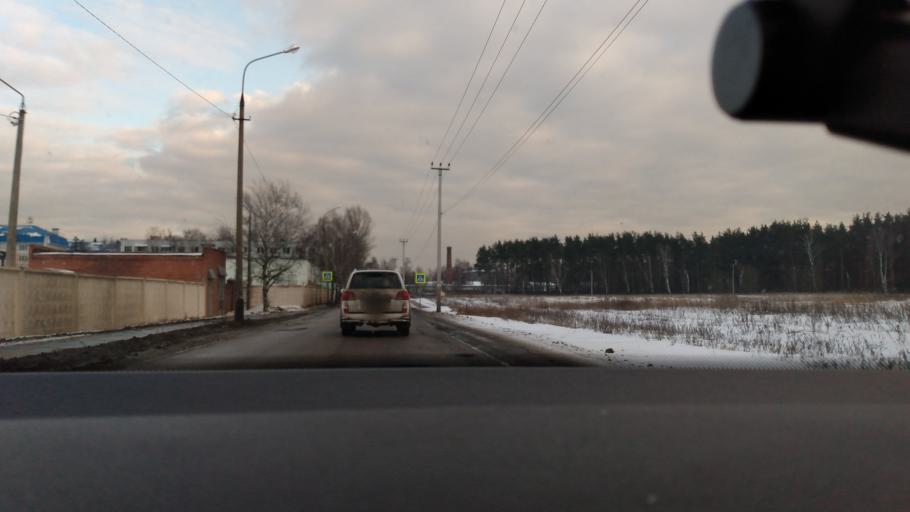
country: RU
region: Moskovskaya
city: Rodniki
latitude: 55.6807
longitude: 38.1002
